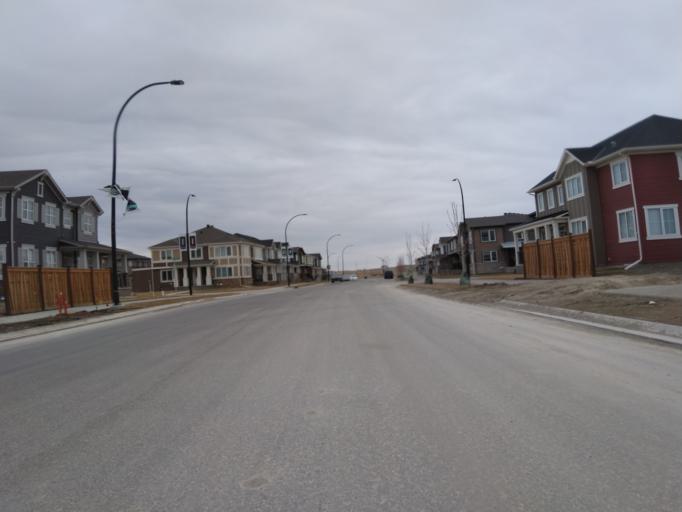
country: CA
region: Alberta
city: Calgary
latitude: 51.1797
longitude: -114.0901
